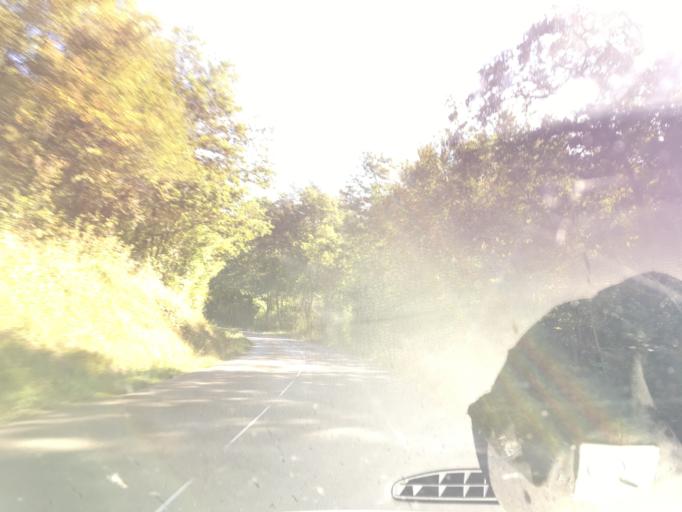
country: FR
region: Bourgogne
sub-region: Departement de l'Yonne
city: Vermenton
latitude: 47.5911
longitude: 3.6887
